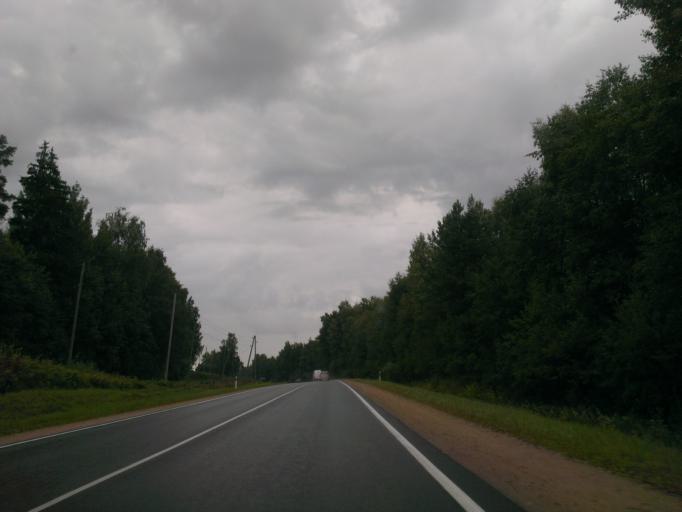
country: LV
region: Kegums
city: Kegums
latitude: 56.7506
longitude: 24.7133
